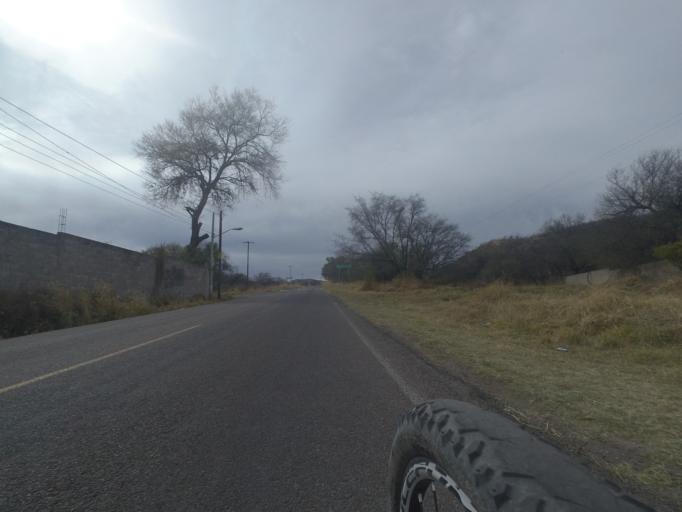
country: MX
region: Aguascalientes
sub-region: Aguascalientes
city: La Loma de los Negritos
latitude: 21.8358
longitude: -102.3699
